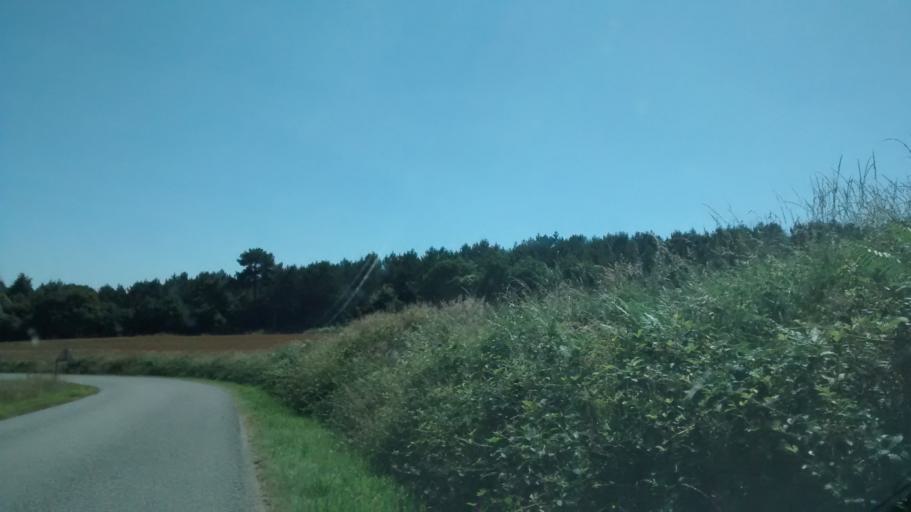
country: FR
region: Brittany
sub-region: Departement du Morbihan
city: Campeneac
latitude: 47.9950
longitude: -2.3026
